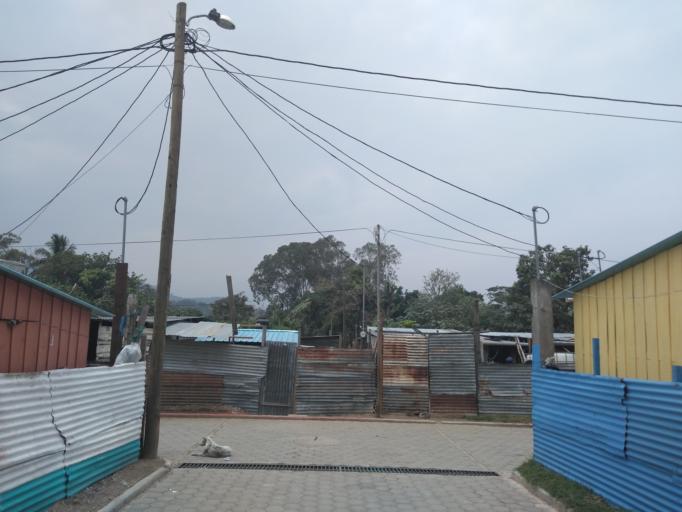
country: GT
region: Guatemala
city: Petapa
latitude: 14.5053
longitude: -90.5492
